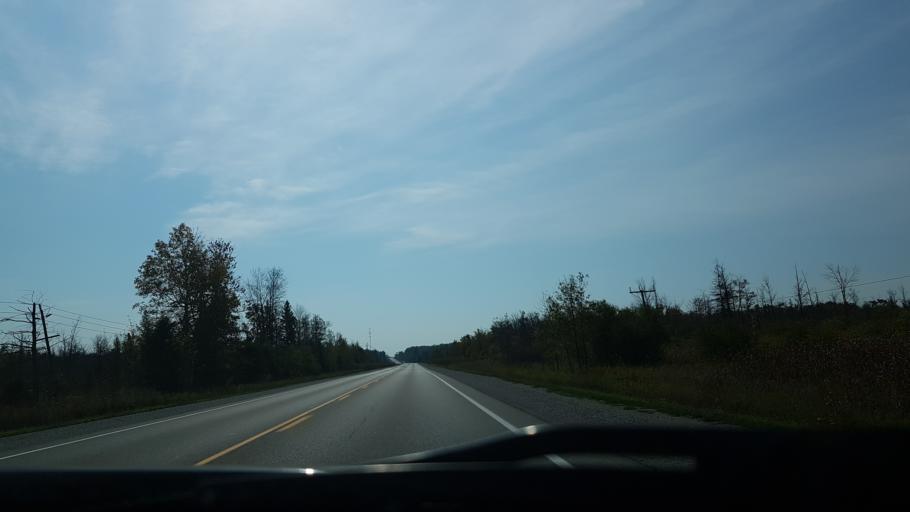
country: CA
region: Ontario
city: Orillia
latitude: 44.7037
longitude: -79.2775
